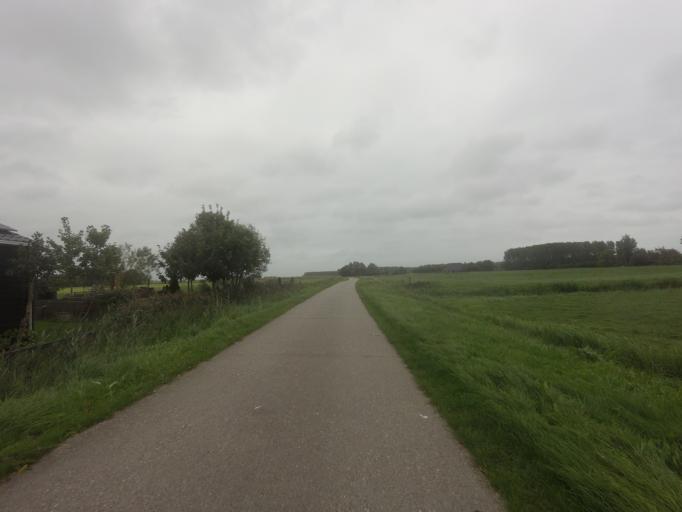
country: NL
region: Friesland
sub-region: Gemeente Leeuwarden
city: Bilgaard
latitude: 53.2277
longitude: 5.7860
